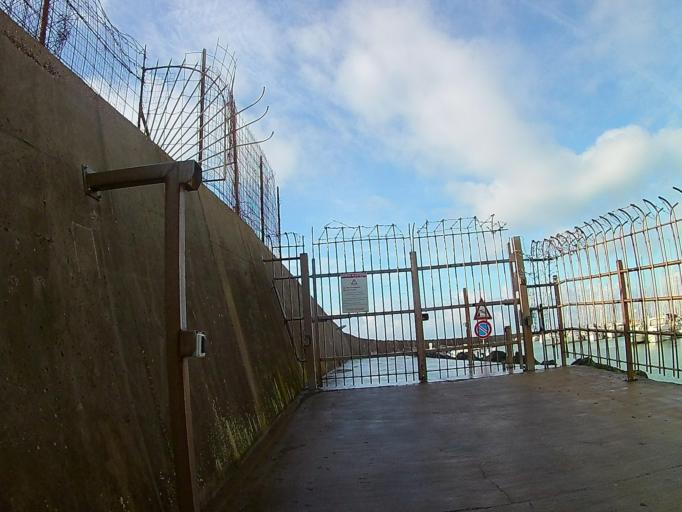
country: IT
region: Latium
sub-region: Citta metropolitana di Roma Capitale
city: Lido di Ostia
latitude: 41.7364
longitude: 12.2521
